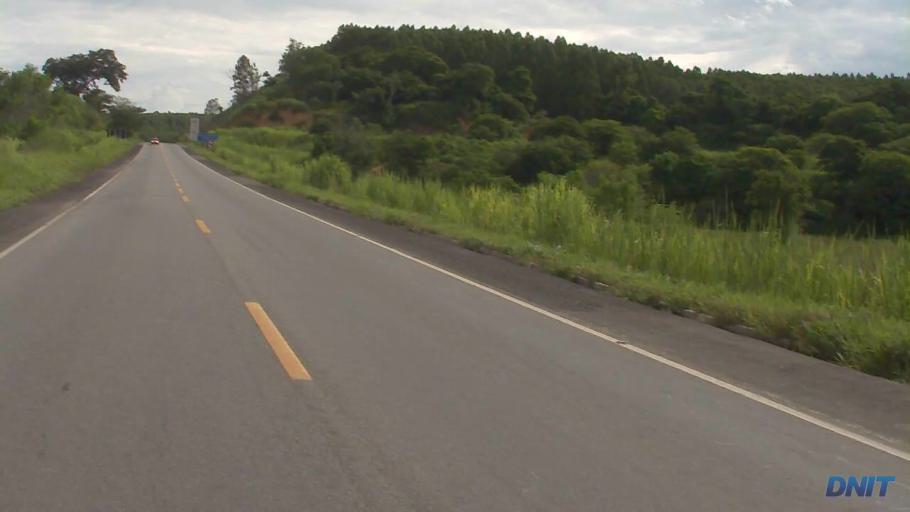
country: BR
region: Minas Gerais
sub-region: Belo Oriente
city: Belo Oriente
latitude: -19.2437
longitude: -42.3364
